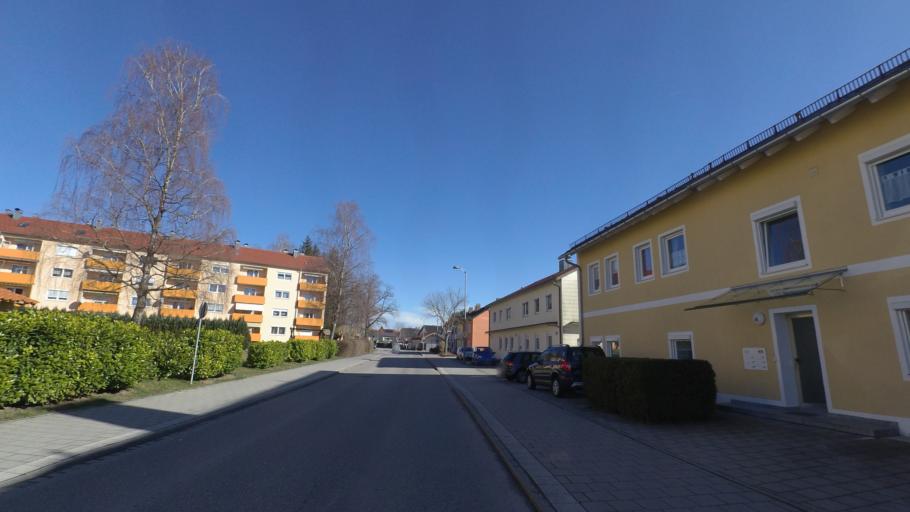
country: DE
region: Bavaria
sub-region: Upper Bavaria
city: Traunreut
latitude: 47.9574
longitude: 12.5902
